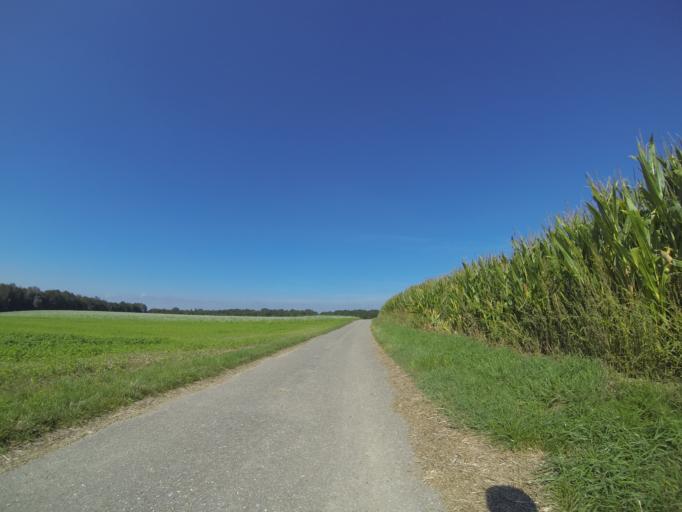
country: DE
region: Baden-Wuerttemberg
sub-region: Tuebingen Region
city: Burgrieden
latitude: 48.2514
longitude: 9.9203
